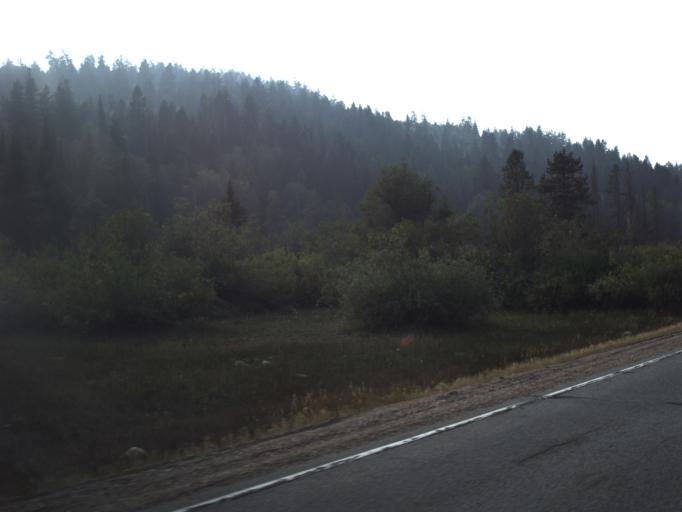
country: US
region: Utah
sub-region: Summit County
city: Francis
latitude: 40.6131
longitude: -111.1273
